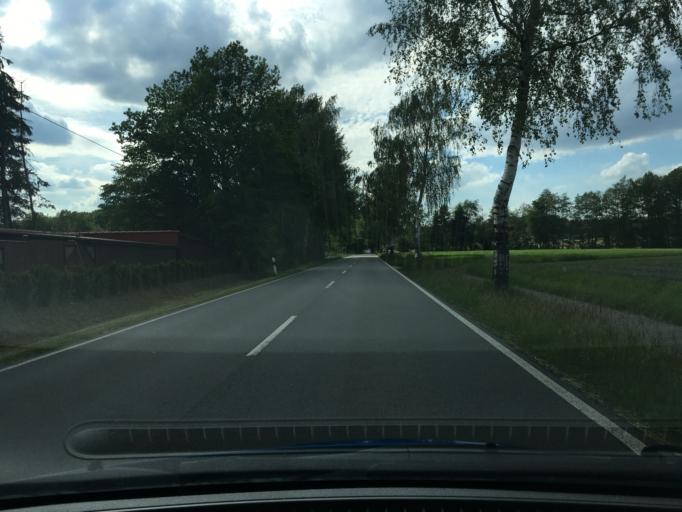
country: DE
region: Lower Saxony
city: Welle
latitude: 53.2485
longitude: 9.7792
